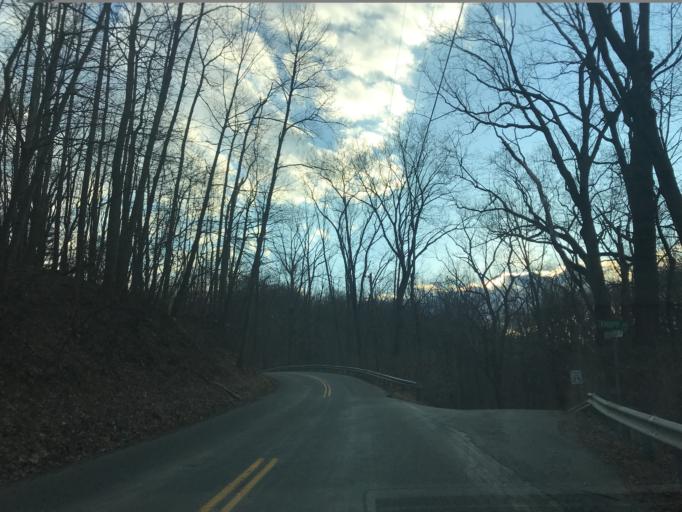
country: US
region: Maryland
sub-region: Harford County
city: Jarrettsville
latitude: 39.6301
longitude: -76.4181
